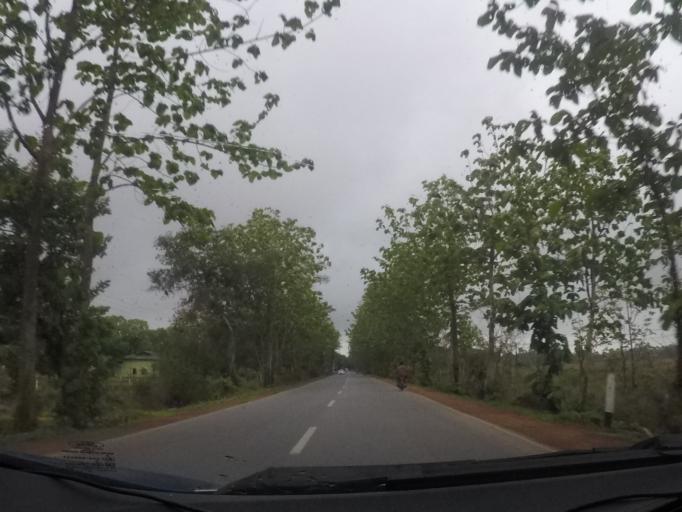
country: MM
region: Bago
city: Paungde
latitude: 18.2608
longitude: 95.6422
